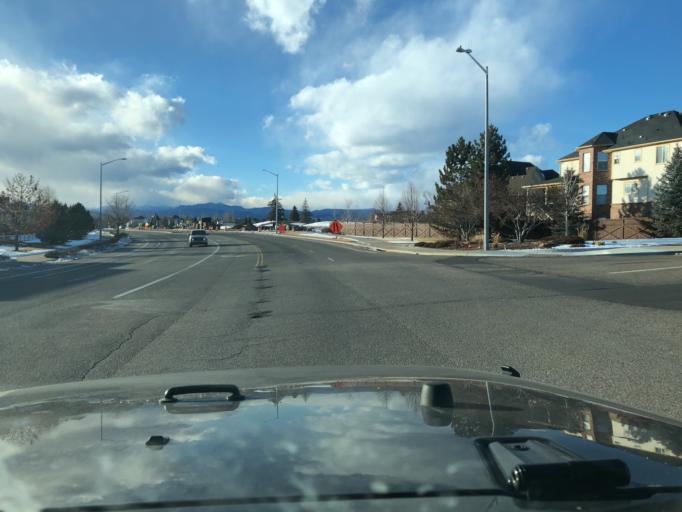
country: US
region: Colorado
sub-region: Boulder County
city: Longmont
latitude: 40.1888
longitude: -105.0609
